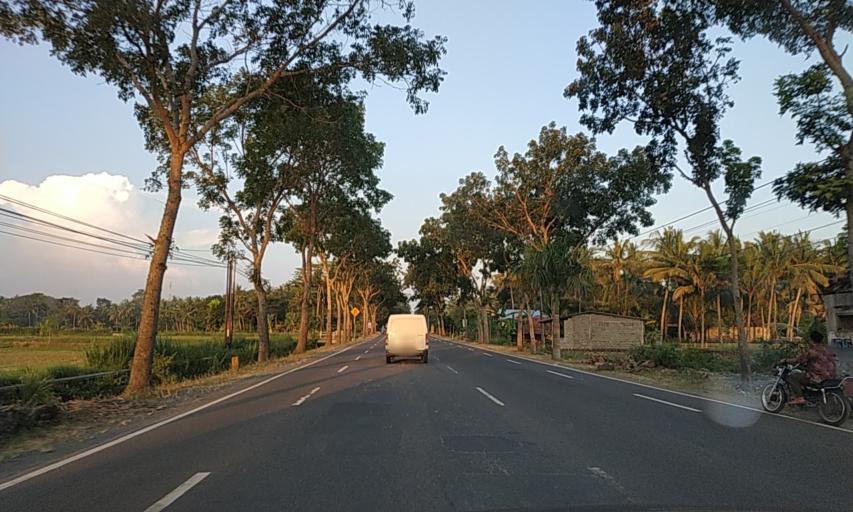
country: ID
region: Daerah Istimewa Yogyakarta
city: Srandakan
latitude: -7.8873
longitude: 110.0861
